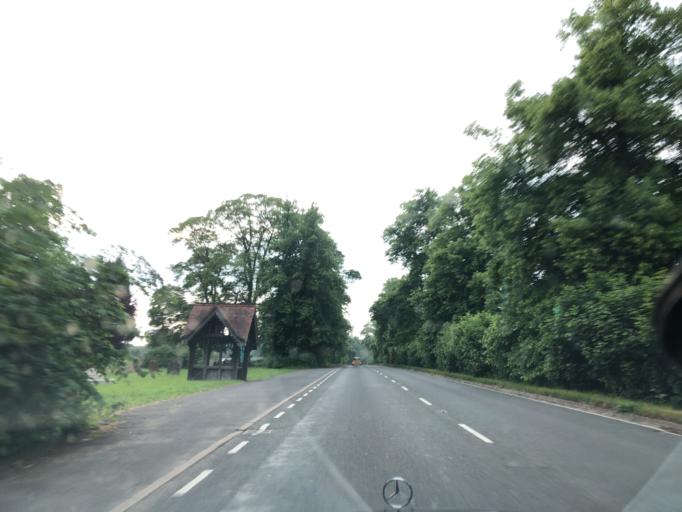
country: GB
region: England
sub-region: Warwickshire
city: Wroxall
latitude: 52.3038
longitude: -1.6542
